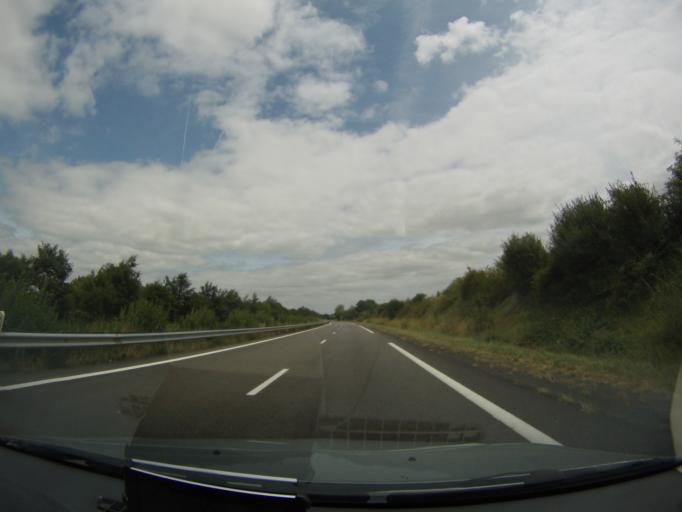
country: FR
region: Pays de la Loire
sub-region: Departement de la Loire-Atlantique
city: Le Pallet
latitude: 47.1560
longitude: -1.3128
